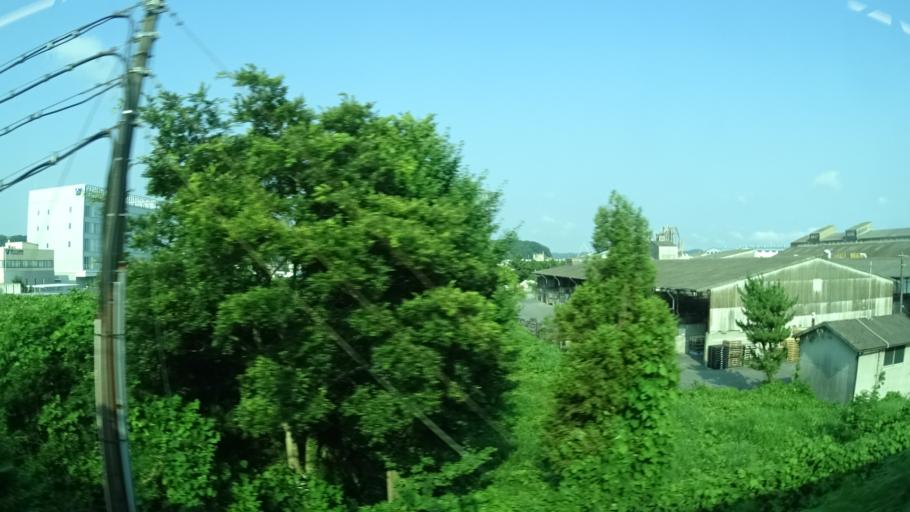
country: JP
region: Fukushima
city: Iwaki
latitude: 36.9834
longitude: 140.8632
